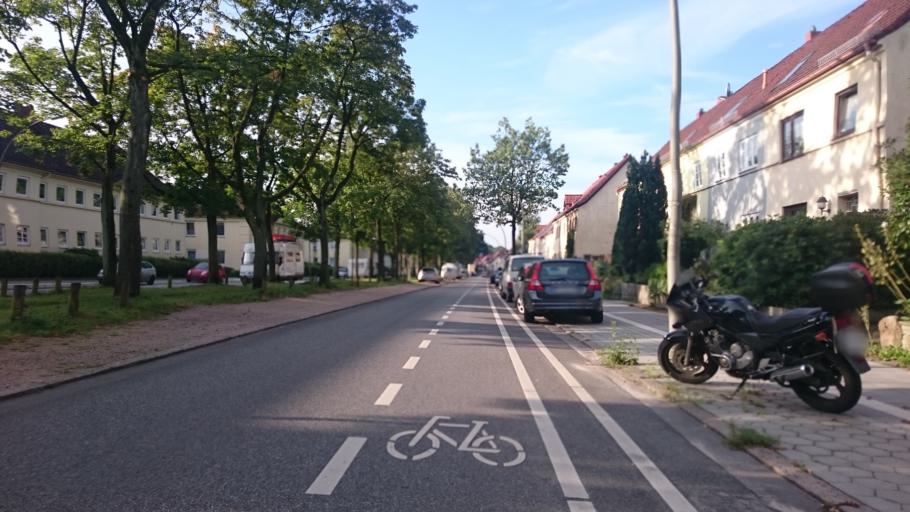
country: DE
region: Hamburg
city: Eidelstedt
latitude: 53.5715
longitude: 9.8904
